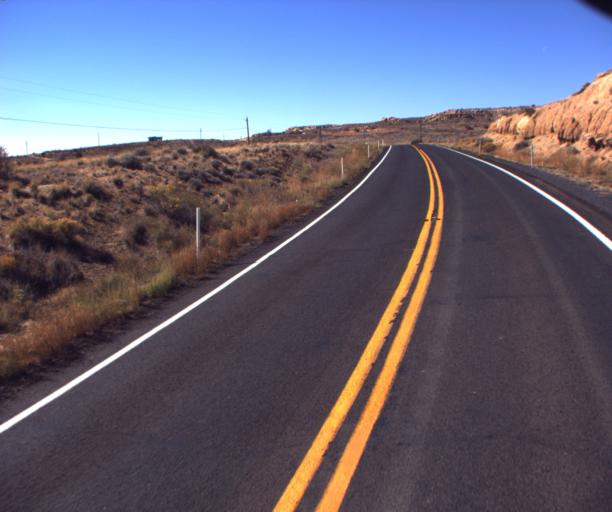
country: US
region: Arizona
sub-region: Navajo County
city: First Mesa
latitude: 35.8858
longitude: -110.6304
